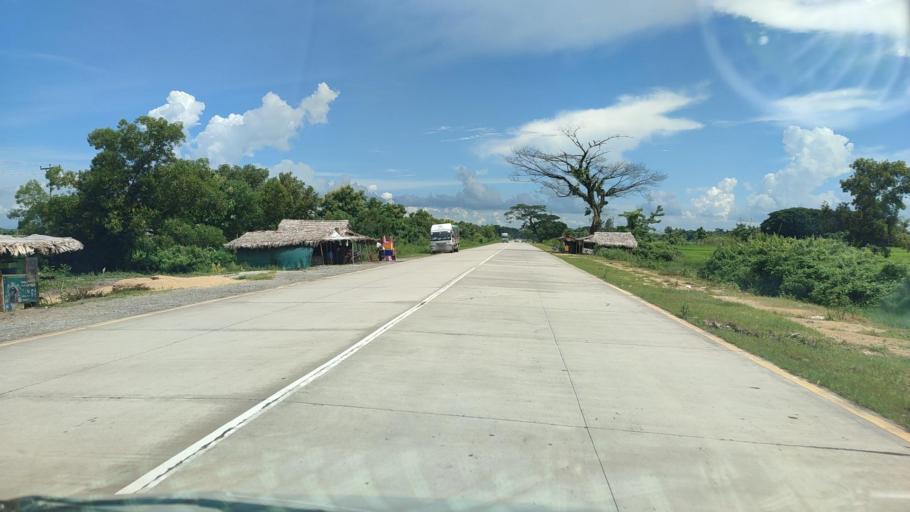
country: MM
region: Bago
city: Nyaunglebin
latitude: 17.9755
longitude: 96.7093
